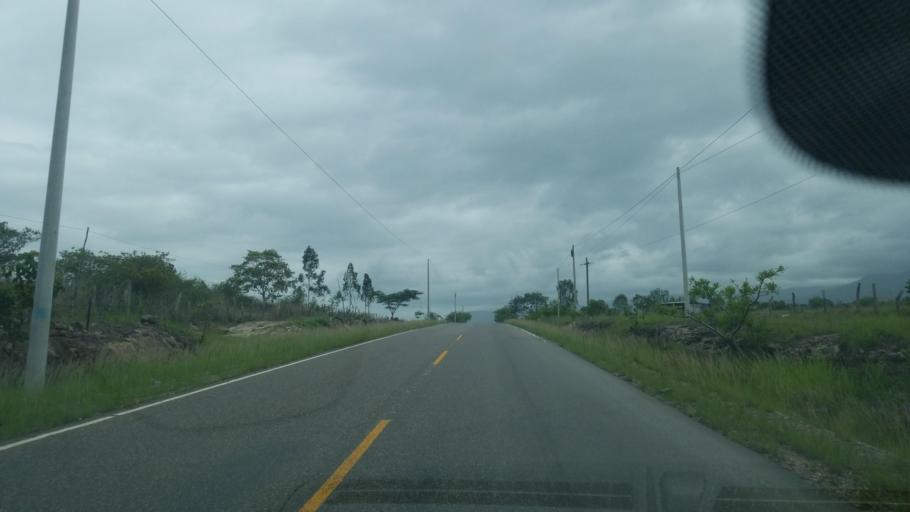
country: HN
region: Ocotepeque
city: Lucerna
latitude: 14.5334
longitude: -88.9496
